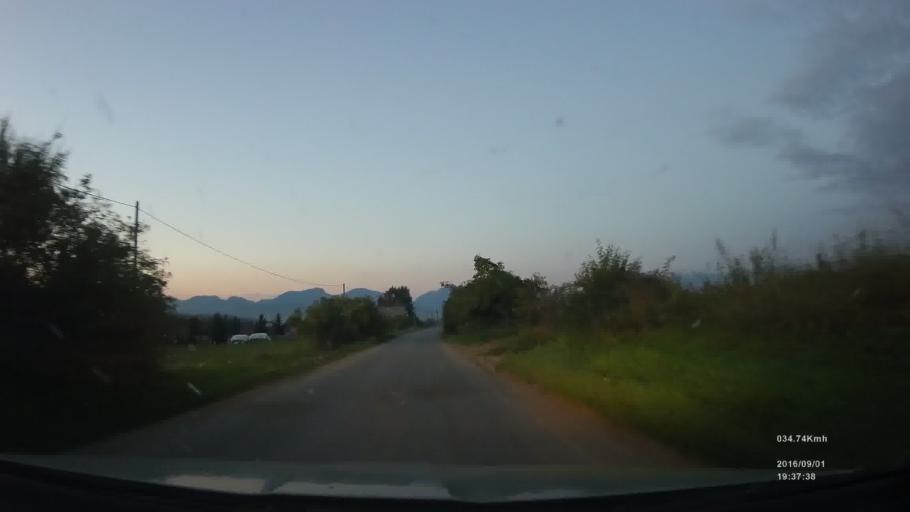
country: SK
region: Zilinsky
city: Ruzomberok
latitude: 49.0461
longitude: 19.4288
